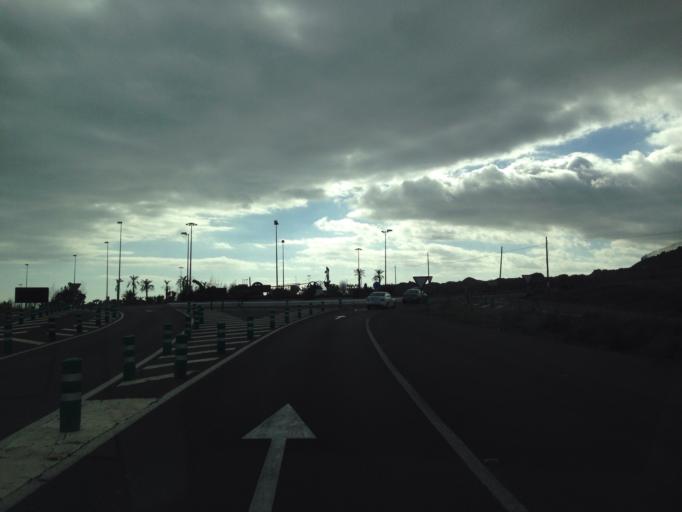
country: ES
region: Canary Islands
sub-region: Provincia de Las Palmas
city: Cruce de Arinaga
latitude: 27.8274
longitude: -15.4549
